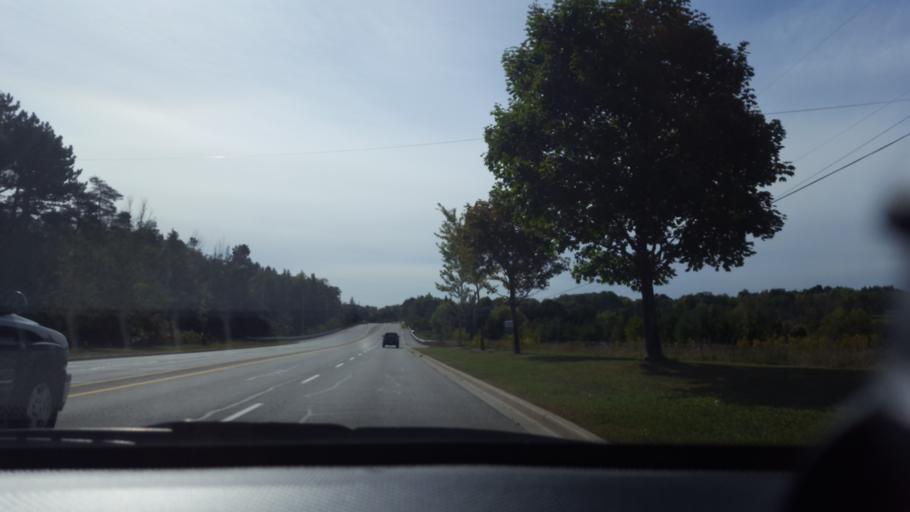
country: CA
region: Ontario
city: Newmarket
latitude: 44.0187
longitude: -79.5004
